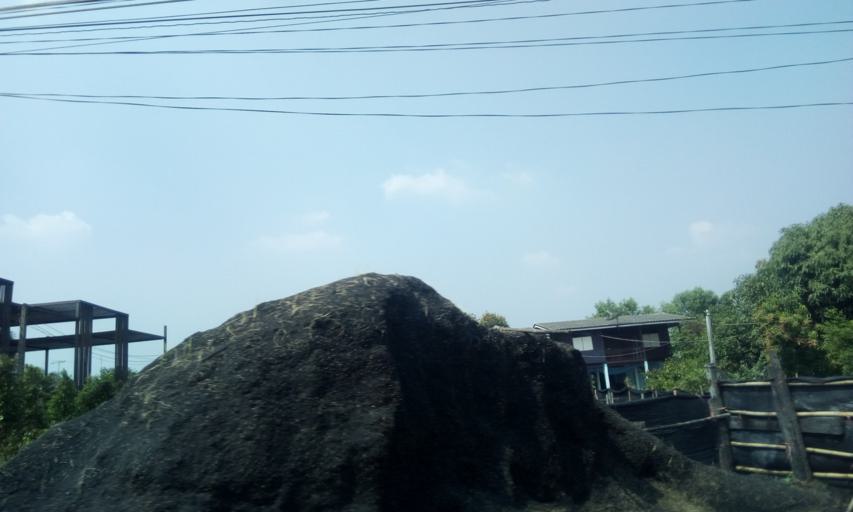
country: TH
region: Nakhon Nayok
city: Ongkharak
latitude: 14.1329
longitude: 100.9576
